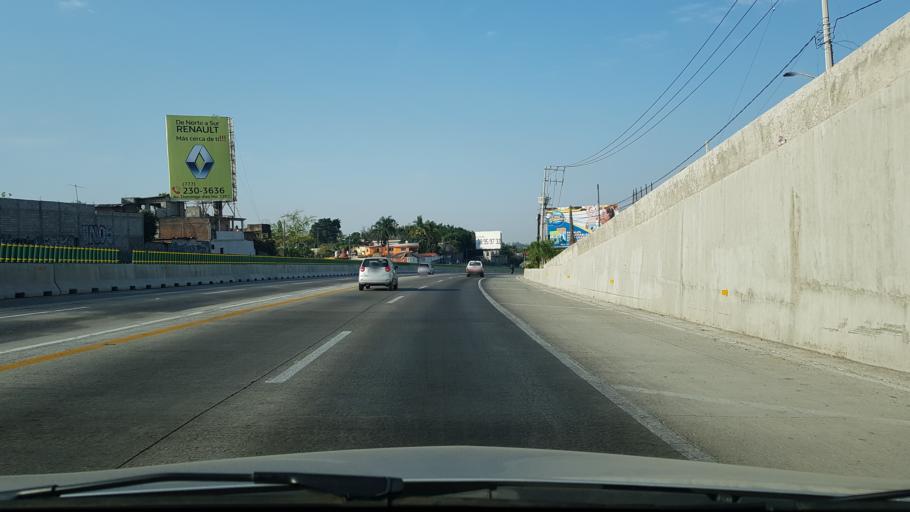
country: MX
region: Morelos
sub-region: Cuernavaca
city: Cuernavaca
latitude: 18.9115
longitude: -99.2072
